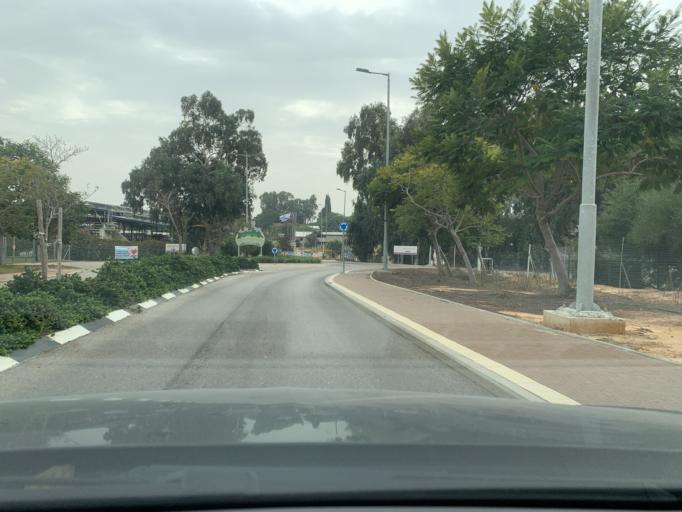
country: IL
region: Central District
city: Tirah
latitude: 32.2211
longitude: 34.9391
